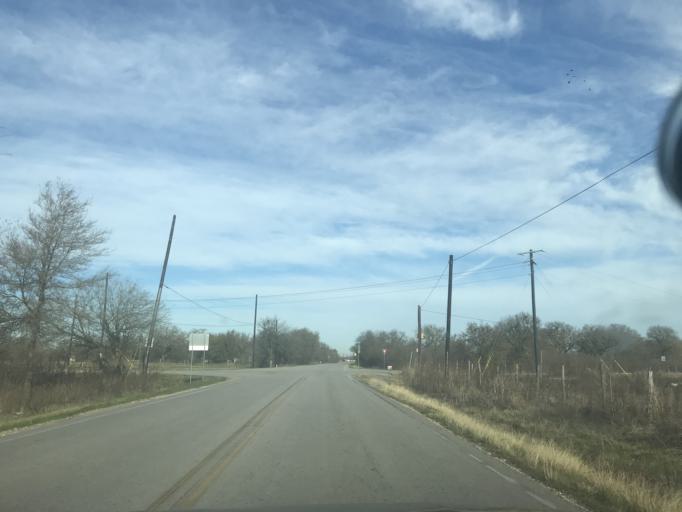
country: US
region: Texas
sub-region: Travis County
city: Manor
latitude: 30.3002
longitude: -97.5280
